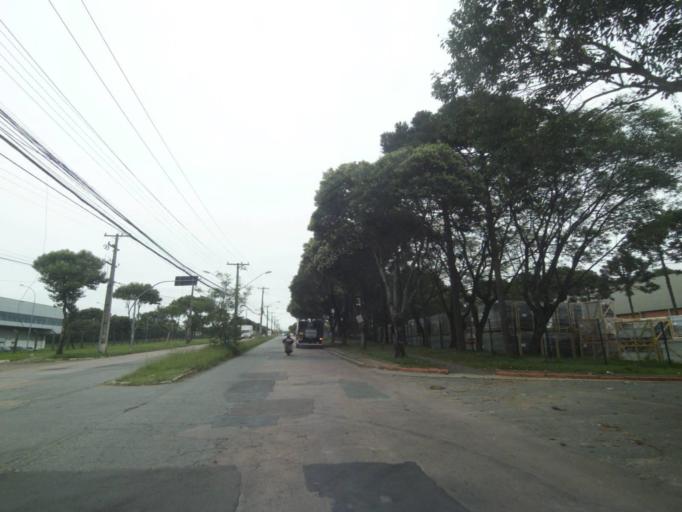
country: BR
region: Parana
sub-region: Sao Jose Dos Pinhais
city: Sao Jose dos Pinhais
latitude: -25.5297
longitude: -49.3138
